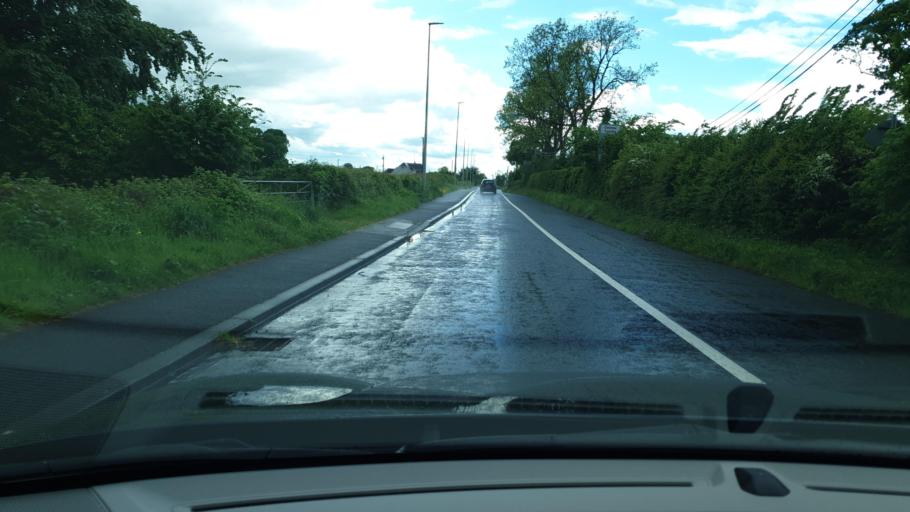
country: IE
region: Connaught
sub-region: County Galway
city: Ballinasloe
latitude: 53.3203
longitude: -8.1818
